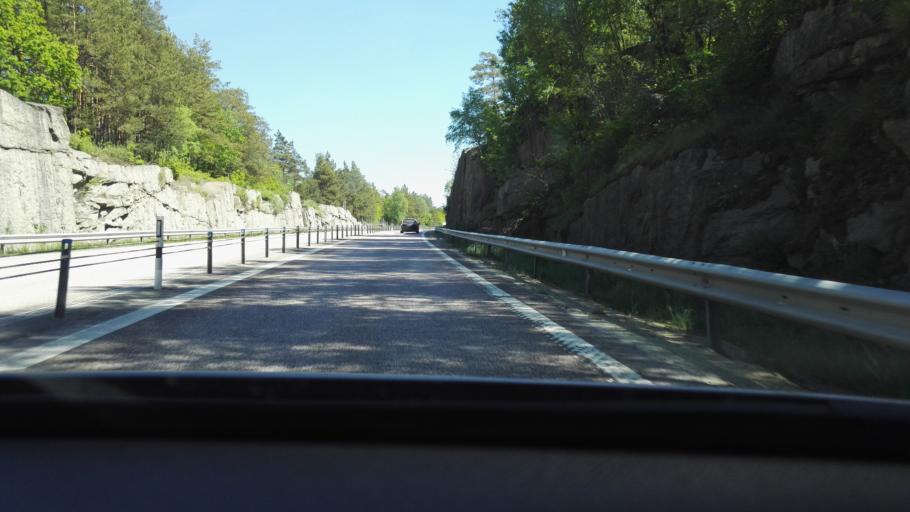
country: SE
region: Blekinge
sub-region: Ronneby Kommun
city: Kallinge
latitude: 56.2134
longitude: 15.3133
